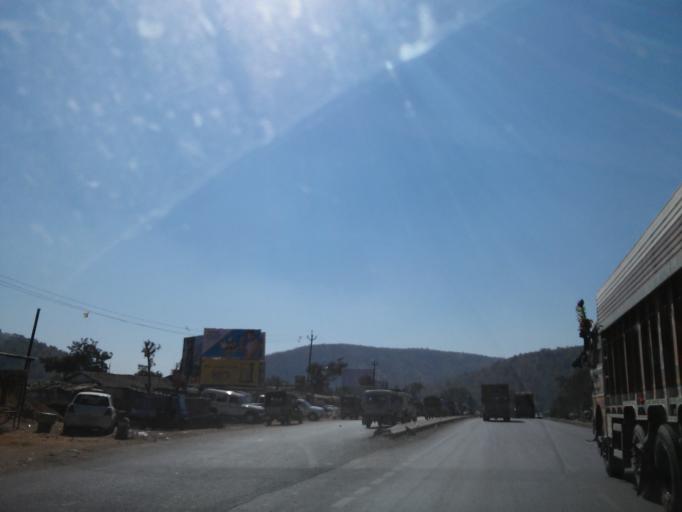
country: IN
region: Gujarat
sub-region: Sabar Kantha
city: Meghraj
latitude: 23.6940
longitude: 73.3871
